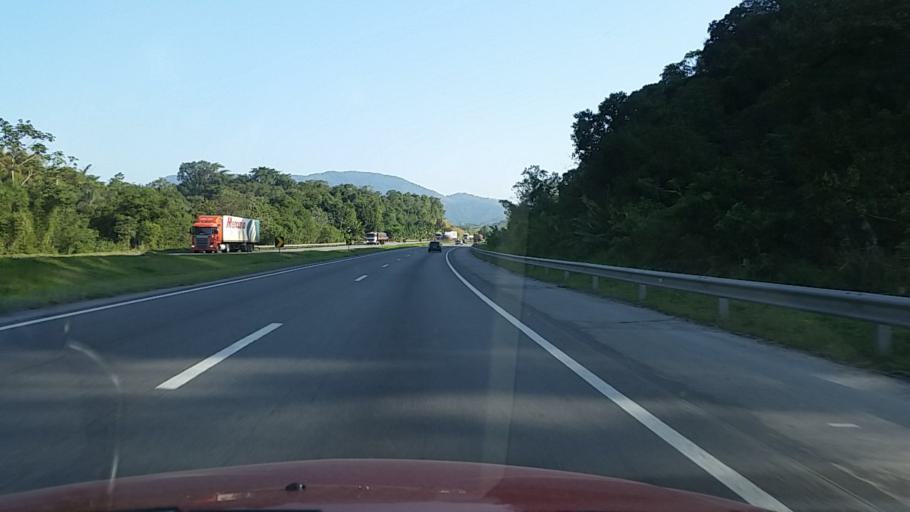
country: BR
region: Sao Paulo
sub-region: Miracatu
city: Miracatu
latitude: -24.2370
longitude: -47.3610
